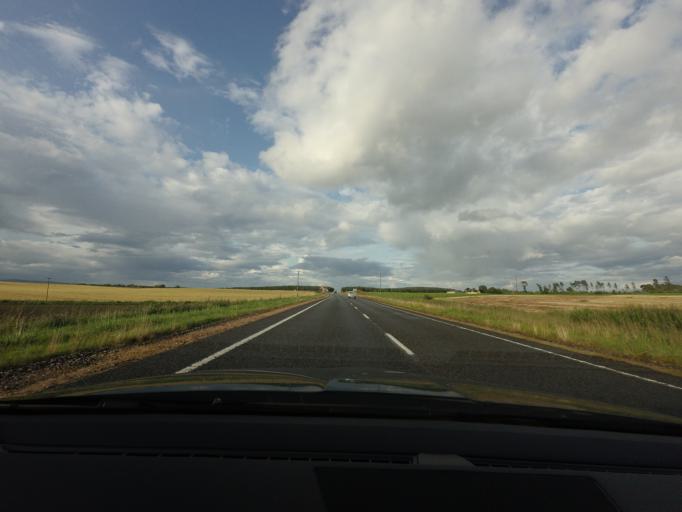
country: GB
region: Scotland
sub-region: Highland
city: Fortrose
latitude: 57.5427
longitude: -4.0091
